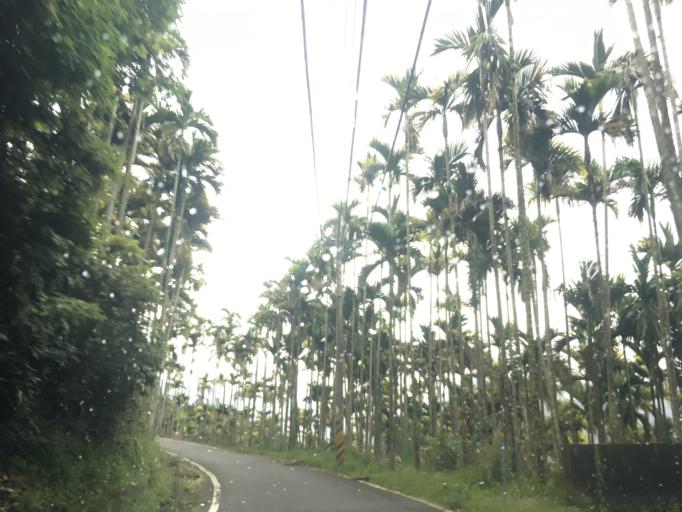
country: TW
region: Taiwan
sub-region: Yunlin
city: Douliu
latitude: 23.5660
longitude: 120.6279
